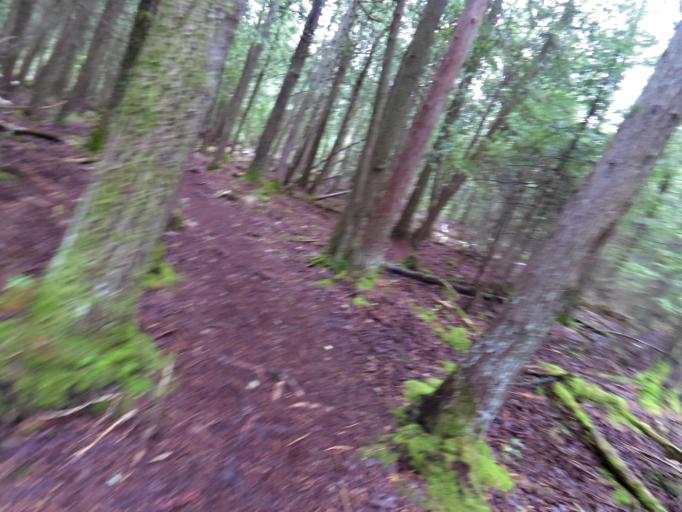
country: CA
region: Ontario
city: Tobermory
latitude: 45.2601
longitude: -81.6487
